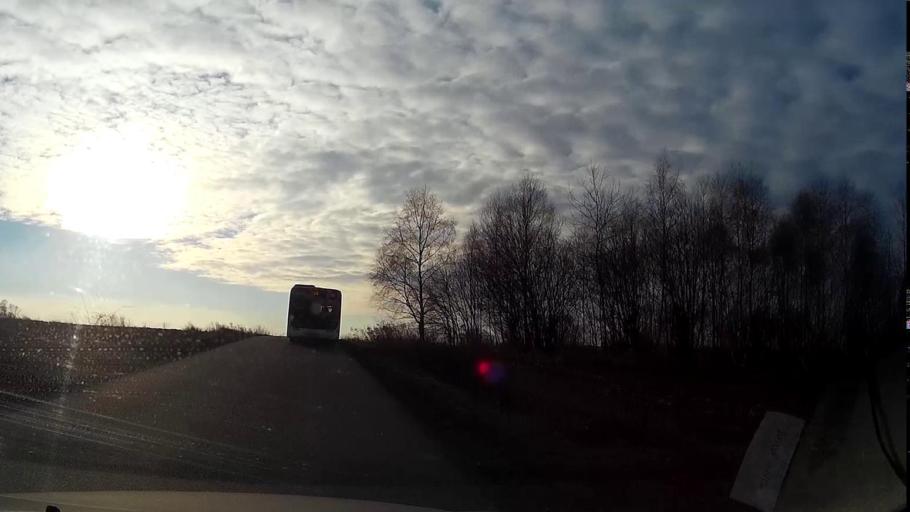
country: PL
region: Lesser Poland Voivodeship
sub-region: Powiat krakowski
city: Sanka
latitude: 50.0633
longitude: 19.6723
